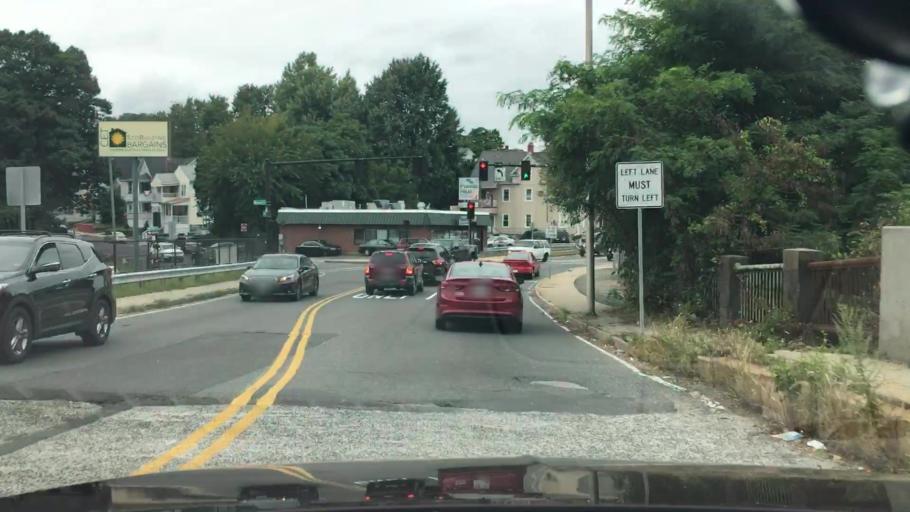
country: US
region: Massachusetts
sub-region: Hampden County
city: Springfield
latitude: 42.1156
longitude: -72.5819
